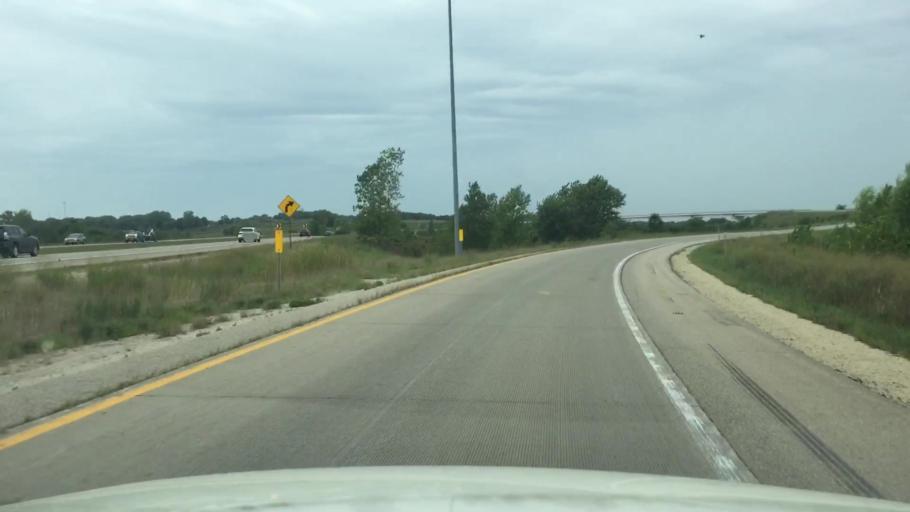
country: US
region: Iowa
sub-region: Polk County
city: West Des Moines
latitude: 41.5231
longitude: -93.7647
